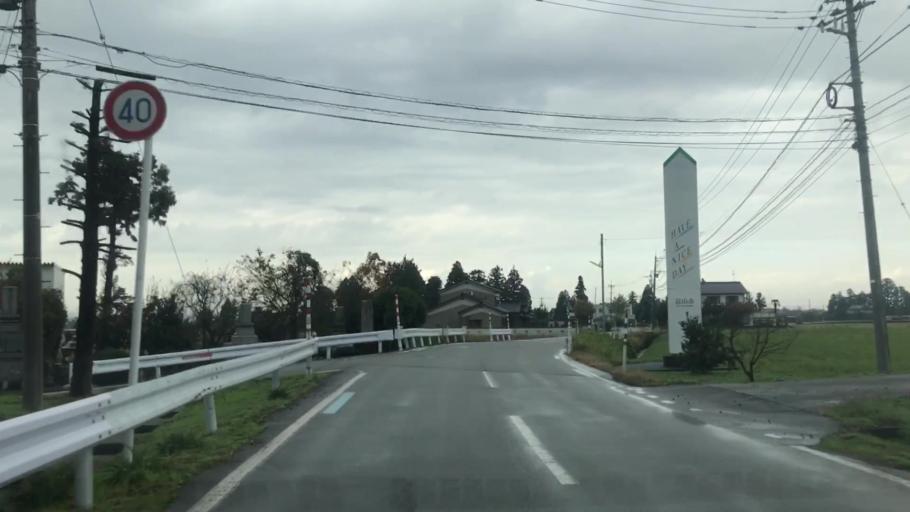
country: JP
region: Toyama
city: Toyama-shi
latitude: 36.6087
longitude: 137.2597
